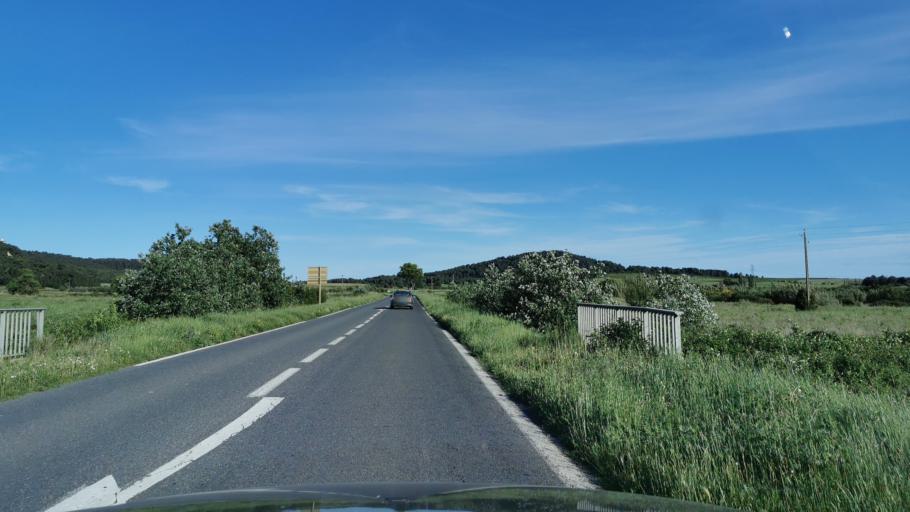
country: FR
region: Languedoc-Roussillon
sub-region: Departement de l'Aude
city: Marcorignan
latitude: 43.2156
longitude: 2.9318
